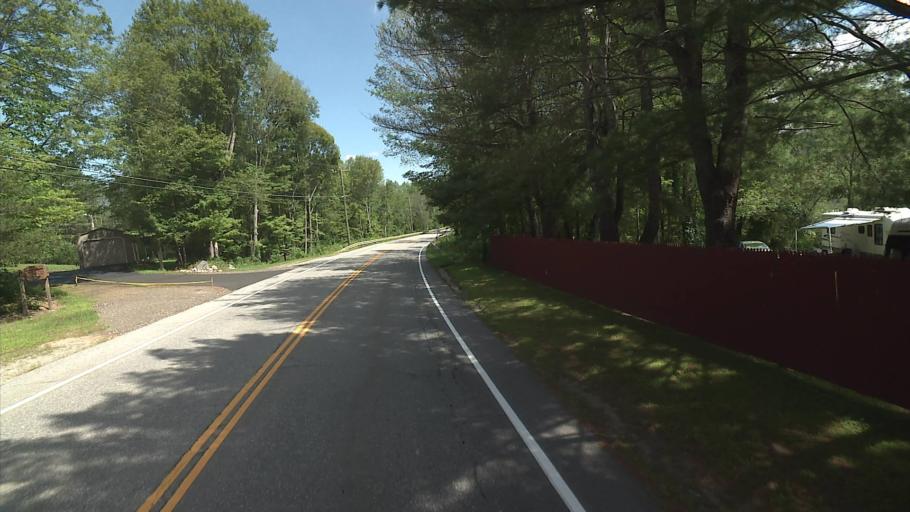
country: US
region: Connecticut
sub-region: Windham County
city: South Woodstock
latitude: 41.8658
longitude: -72.0934
